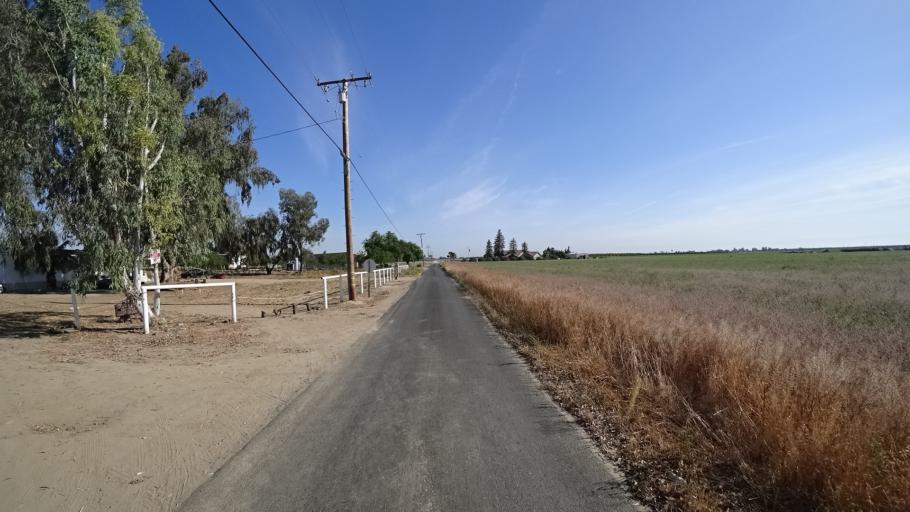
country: US
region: California
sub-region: Kings County
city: Hanford
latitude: 36.3299
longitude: -119.6167
